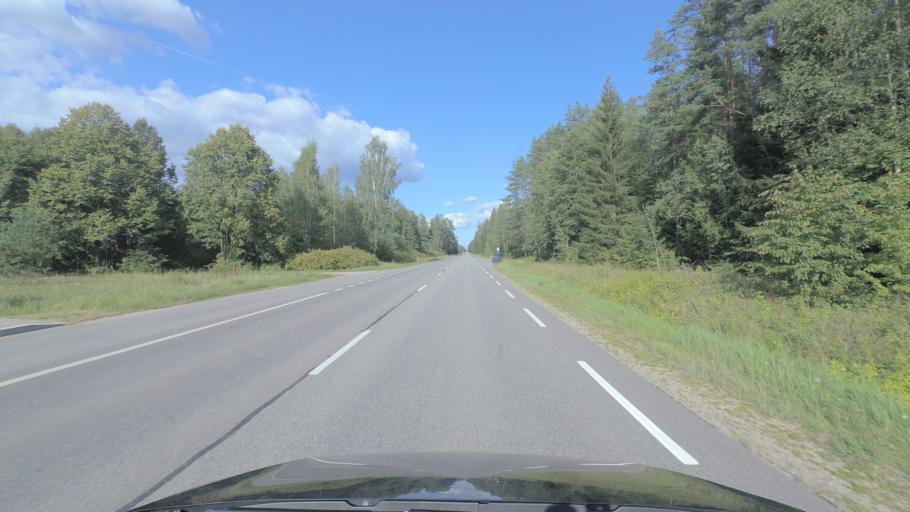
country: LT
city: Pabrade
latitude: 54.9568
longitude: 25.6825
